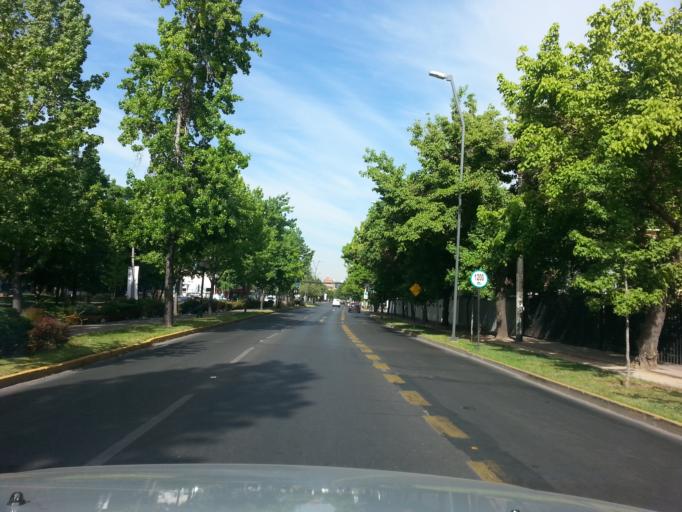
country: CL
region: Santiago Metropolitan
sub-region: Provincia de Santiago
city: Villa Presidente Frei, Nunoa, Santiago, Chile
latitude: -33.4389
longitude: -70.6126
